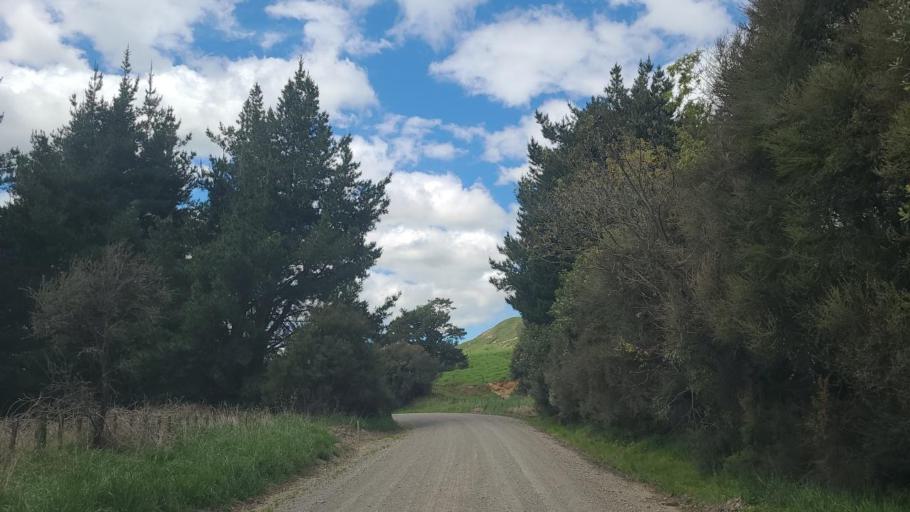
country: NZ
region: Hawke's Bay
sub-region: Napier City
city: Napier
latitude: -39.2221
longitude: 176.7649
